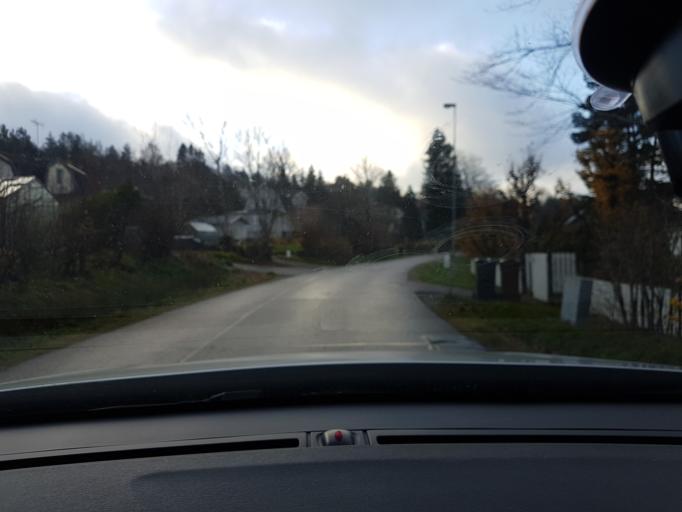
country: SE
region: Vaestra Goetaland
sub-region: Ale Kommun
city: Alafors
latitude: 57.9204
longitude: 12.0738
